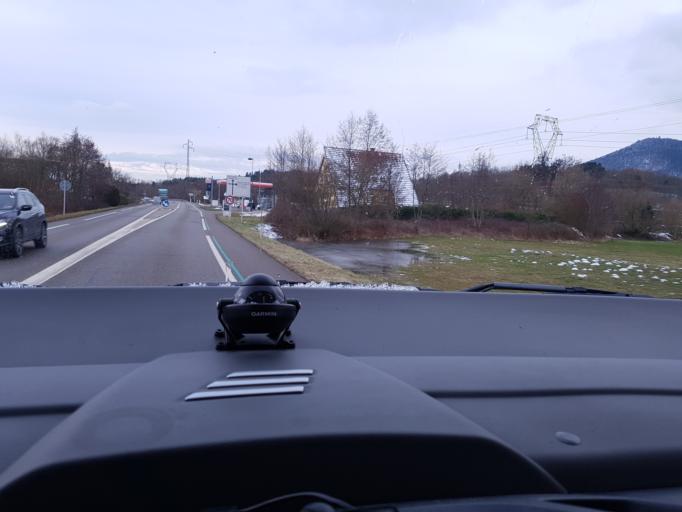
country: FR
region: Alsace
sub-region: Departement du Bas-Rhin
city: Ville
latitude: 48.3266
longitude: 7.3332
